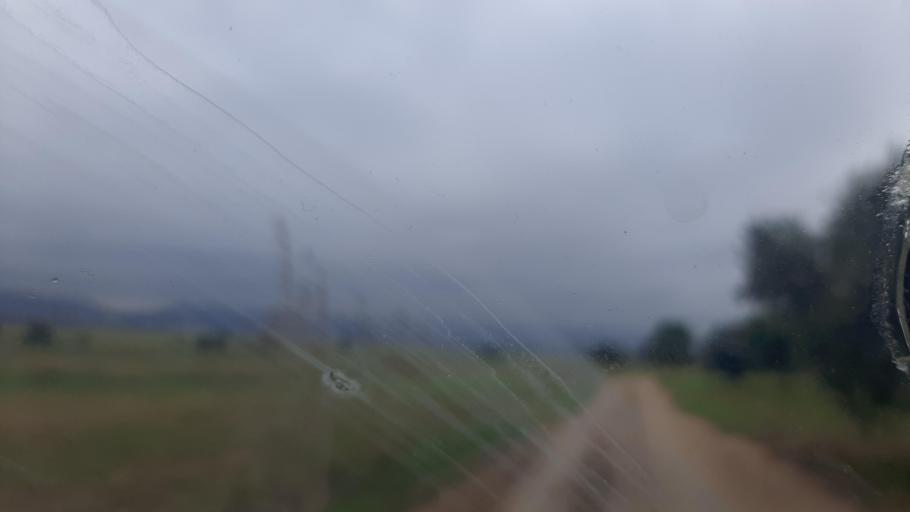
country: TN
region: Tunis
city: La Sebala du Mornag
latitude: 36.5714
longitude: 10.2940
